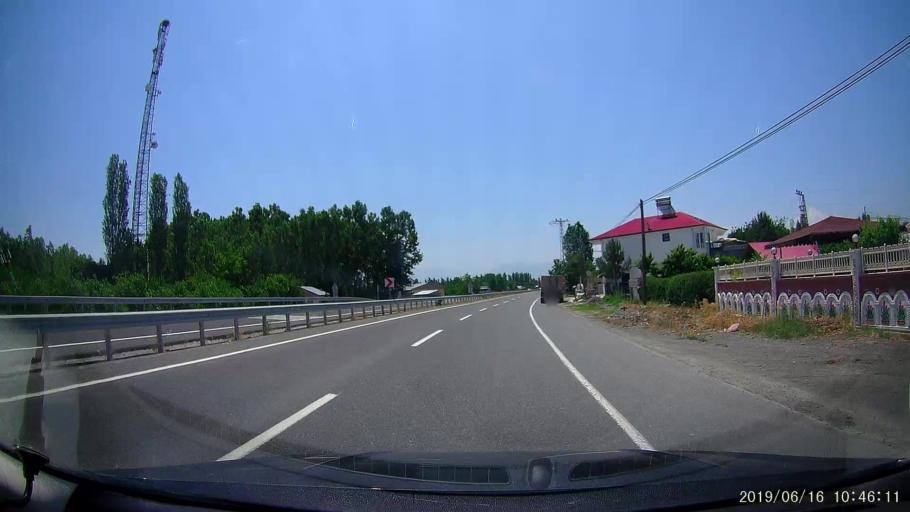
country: AM
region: Armavir
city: Shenavan
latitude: 40.0243
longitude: 43.8776
